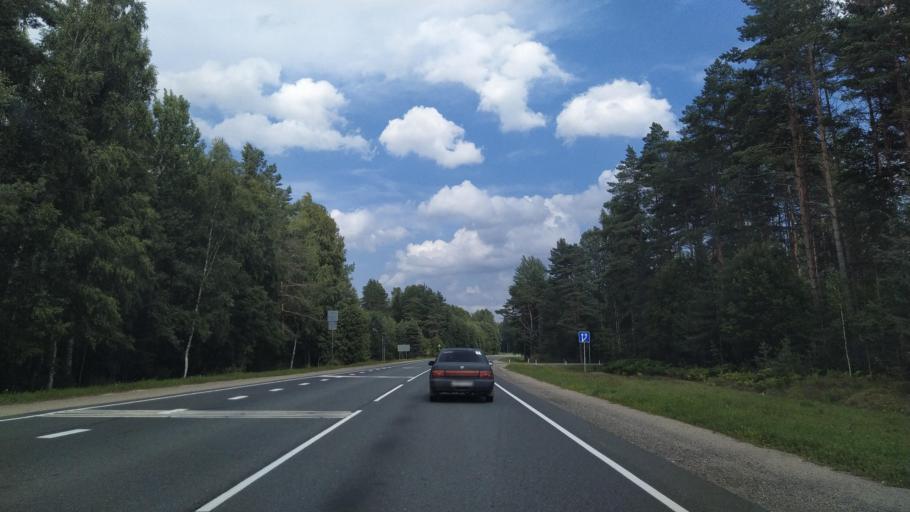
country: RU
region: Pskov
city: Porkhov
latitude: 57.8623
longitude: 29.5773
